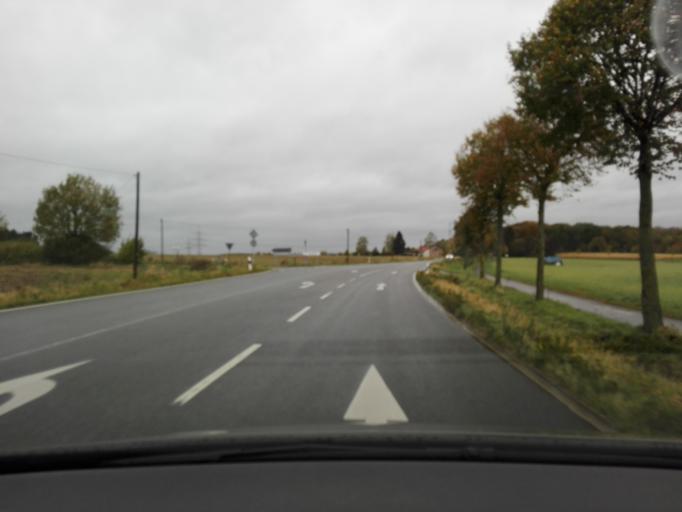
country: DE
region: North Rhine-Westphalia
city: Lunen
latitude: 51.6533
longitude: 7.5030
